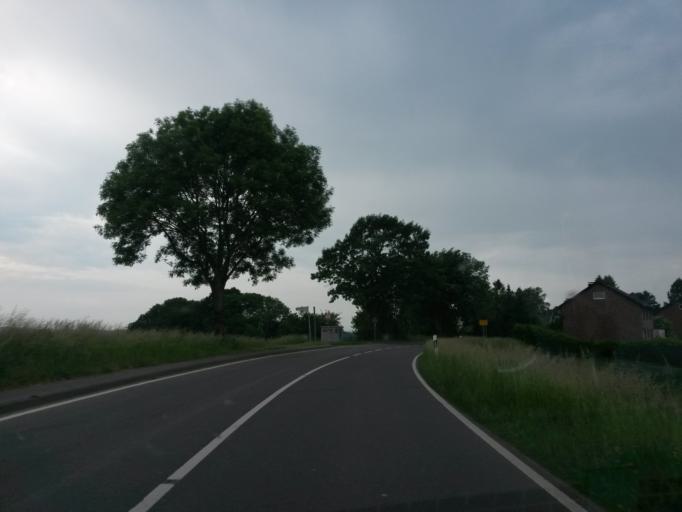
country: DE
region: North Rhine-Westphalia
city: Lohmar
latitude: 50.8876
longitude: 7.2355
